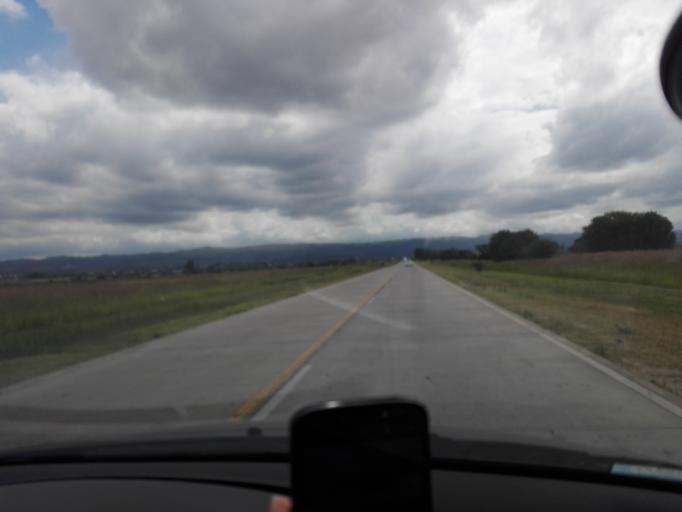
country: AR
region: Cordoba
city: Alta Gracia
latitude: -31.6348
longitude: -64.4100
